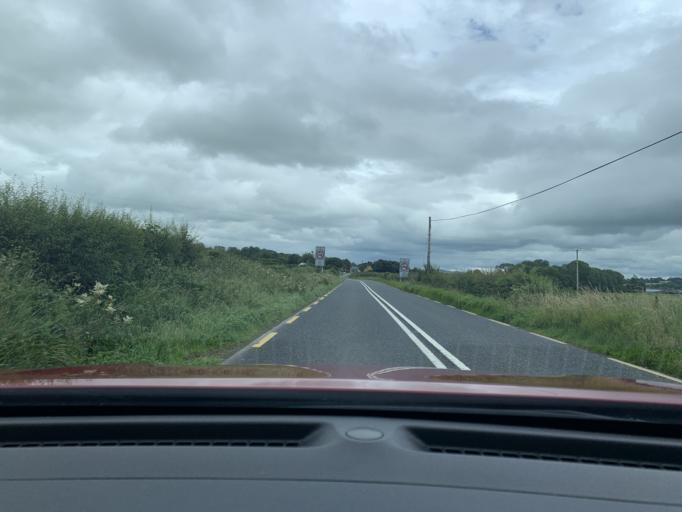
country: IE
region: Ulster
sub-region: County Donegal
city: Convoy
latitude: 54.8006
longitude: -7.6503
